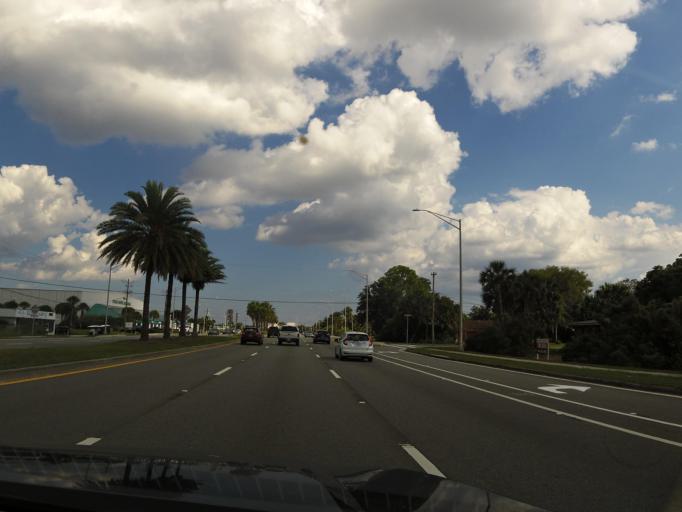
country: US
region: Florida
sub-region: Duval County
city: Jacksonville Beach
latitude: 30.2876
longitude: -81.4337
